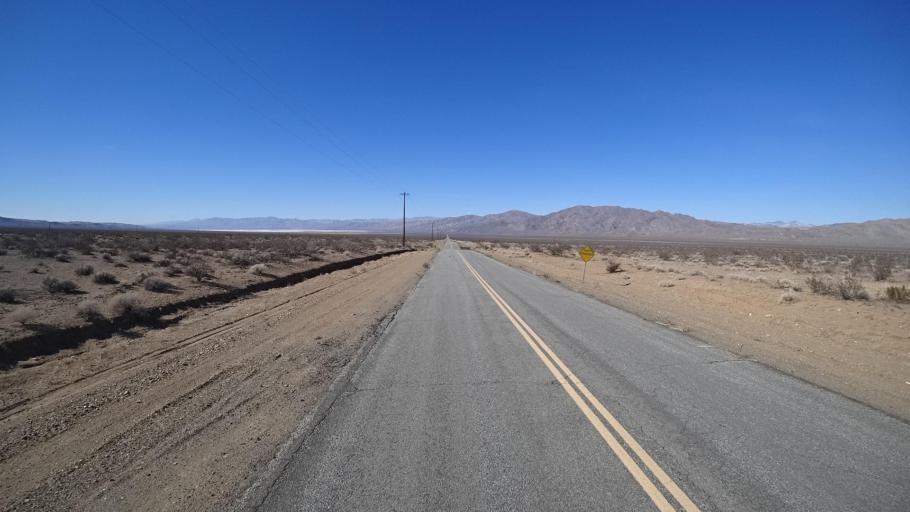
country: US
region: California
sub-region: Kern County
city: Ridgecrest
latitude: 35.3837
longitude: -117.7100
